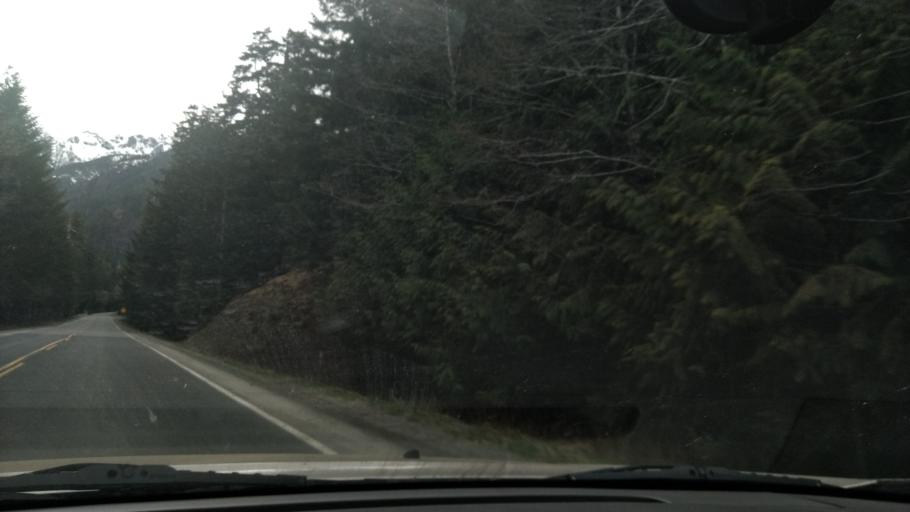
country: CA
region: British Columbia
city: Campbell River
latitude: 49.8429
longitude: -125.8613
